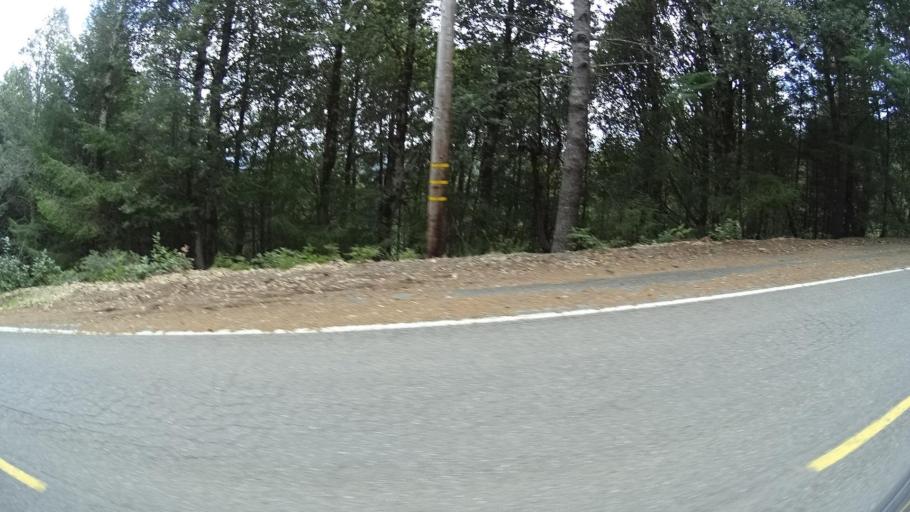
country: US
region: California
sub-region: Humboldt County
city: Redway
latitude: 40.0494
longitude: -124.0186
